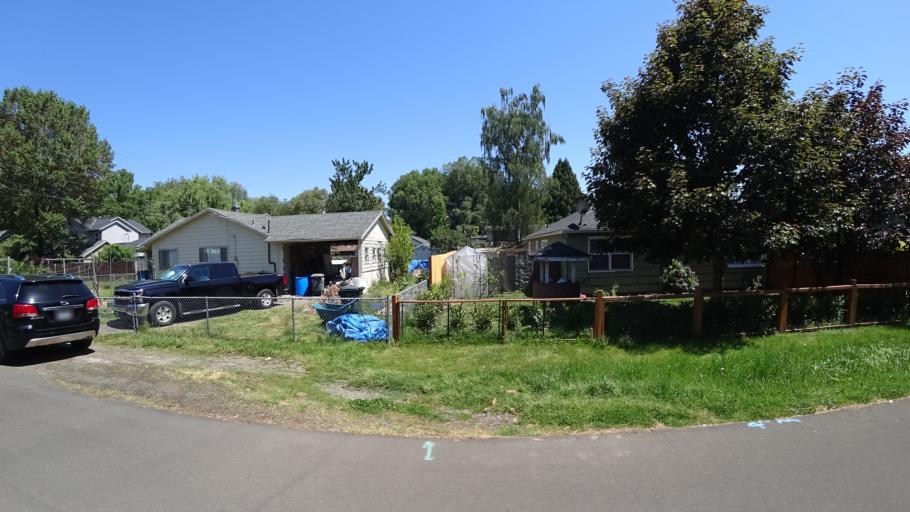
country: US
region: Oregon
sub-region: Washington County
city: Rockcreek
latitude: 45.5271
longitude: -122.9134
